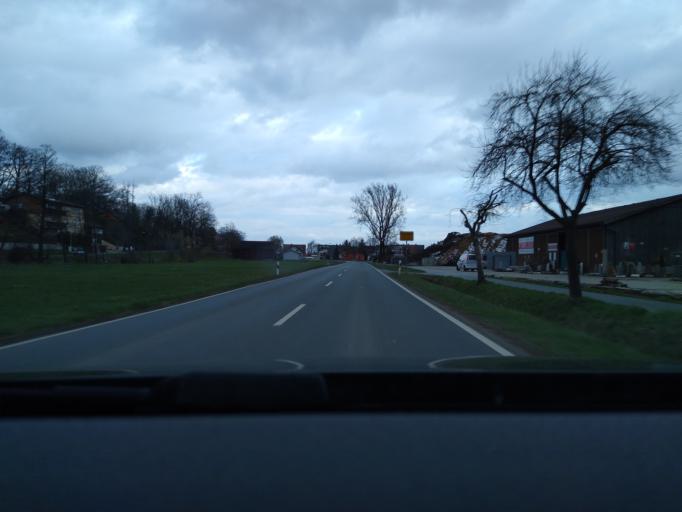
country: DE
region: Bavaria
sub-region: Regierungsbezirk Mittelfranken
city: Zirndorf
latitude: 49.4509
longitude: 10.9220
